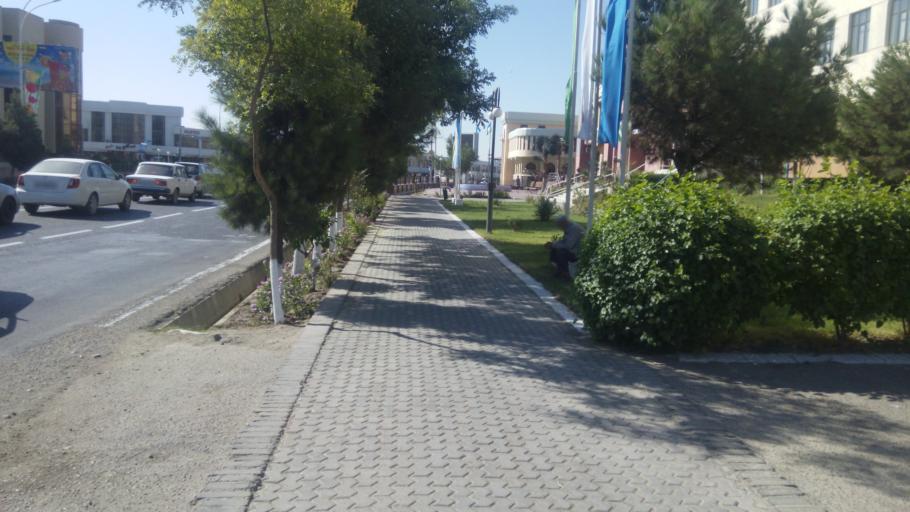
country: UZ
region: Bukhara
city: Bukhara
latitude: 39.7745
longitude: 64.4314
